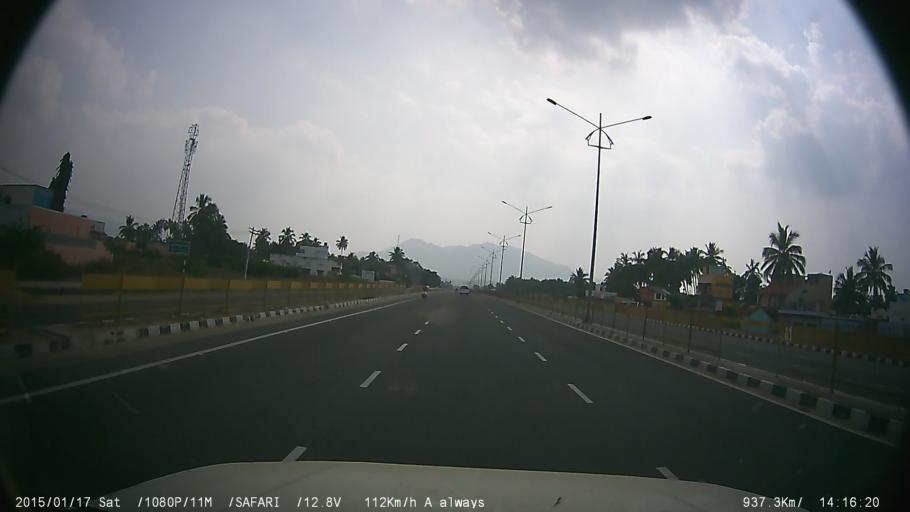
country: IN
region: Tamil Nadu
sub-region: Vellore
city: Ambur
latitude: 12.7561
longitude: 78.6996
